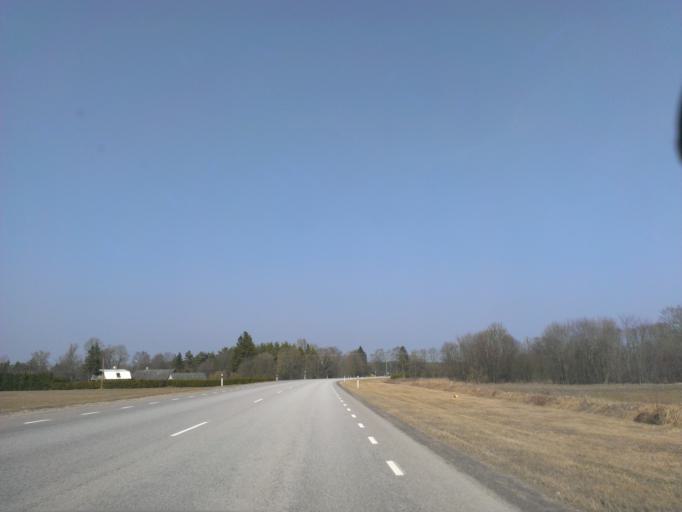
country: EE
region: Saare
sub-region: Orissaare vald
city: Orissaare
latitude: 58.4368
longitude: 22.7875
